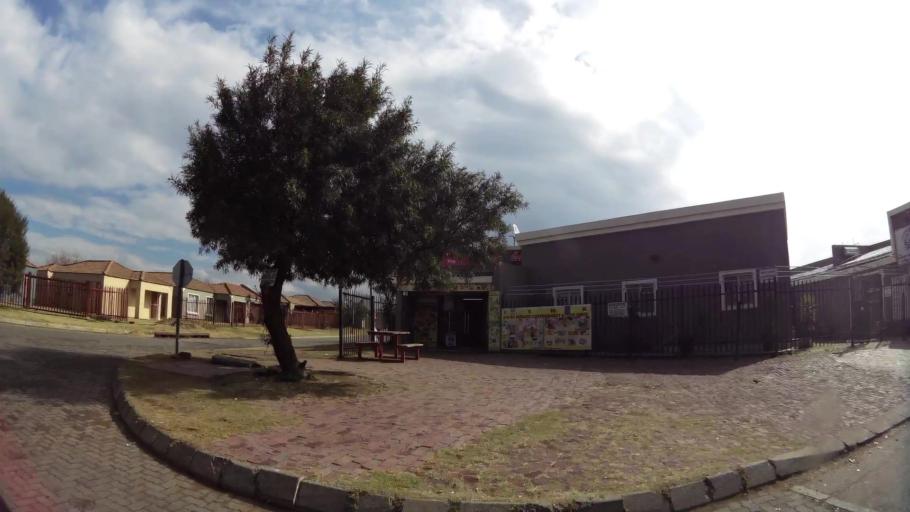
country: ZA
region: Gauteng
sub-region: Sedibeng District Municipality
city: Vanderbijlpark
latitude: -26.7171
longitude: 27.8853
